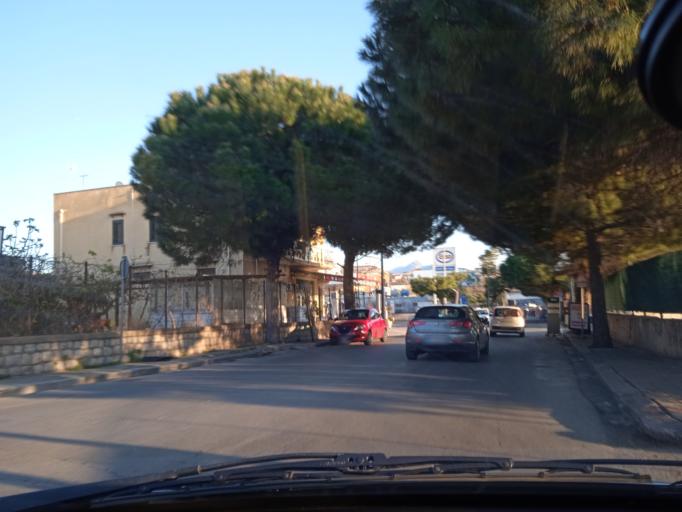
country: IT
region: Sicily
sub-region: Palermo
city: Bagheria
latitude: 38.0893
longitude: 13.5005
